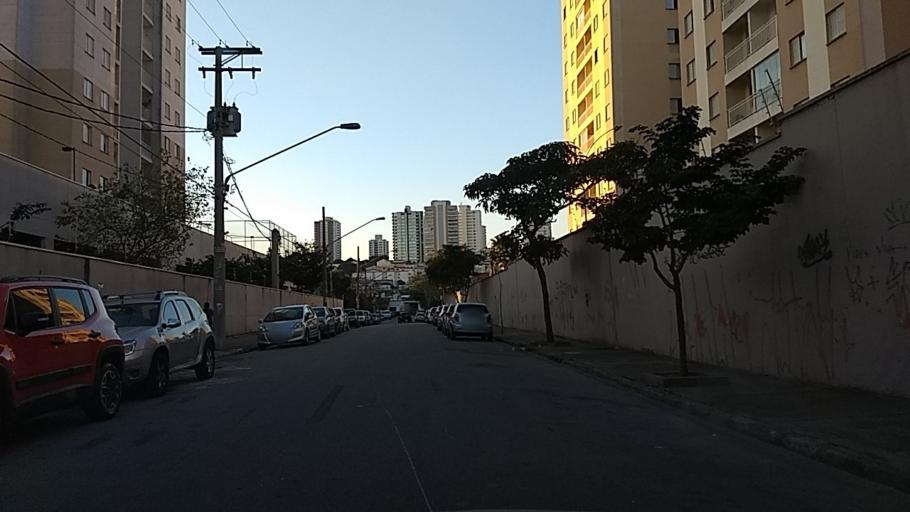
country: BR
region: Sao Paulo
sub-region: Sao Paulo
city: Sao Paulo
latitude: -23.5102
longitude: -46.6033
